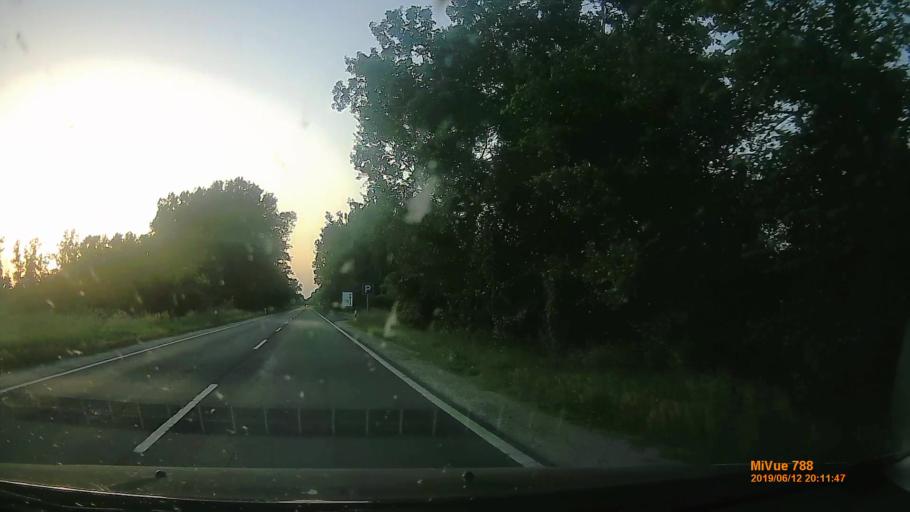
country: HU
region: Pest
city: Ocsa
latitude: 47.2800
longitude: 19.1993
